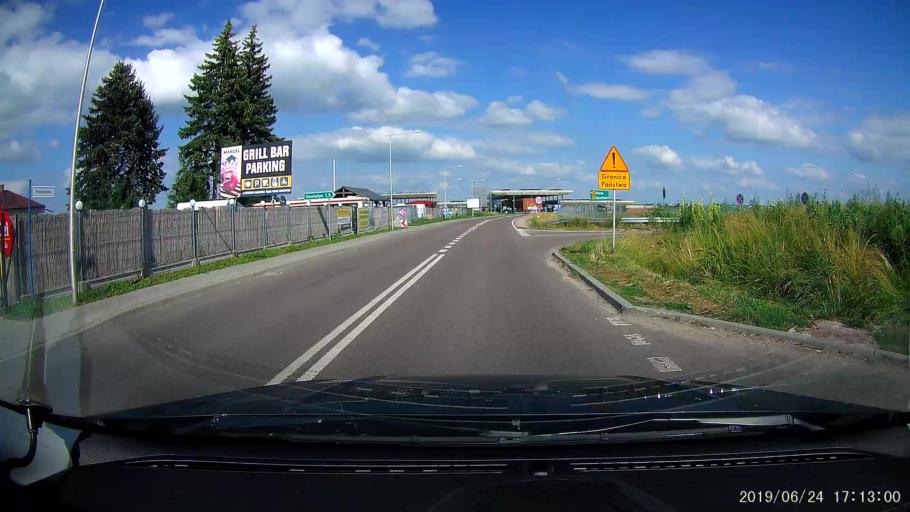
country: PL
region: Lublin Voivodeship
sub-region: Powiat hrubieszowski
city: Dolhobyczow
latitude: 50.5786
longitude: 24.0812
